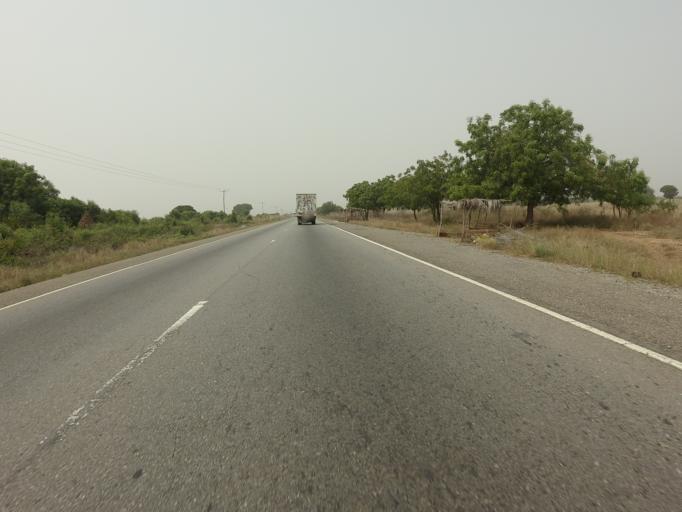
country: GH
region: Volta
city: Anloga
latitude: 5.8871
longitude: 0.4521
